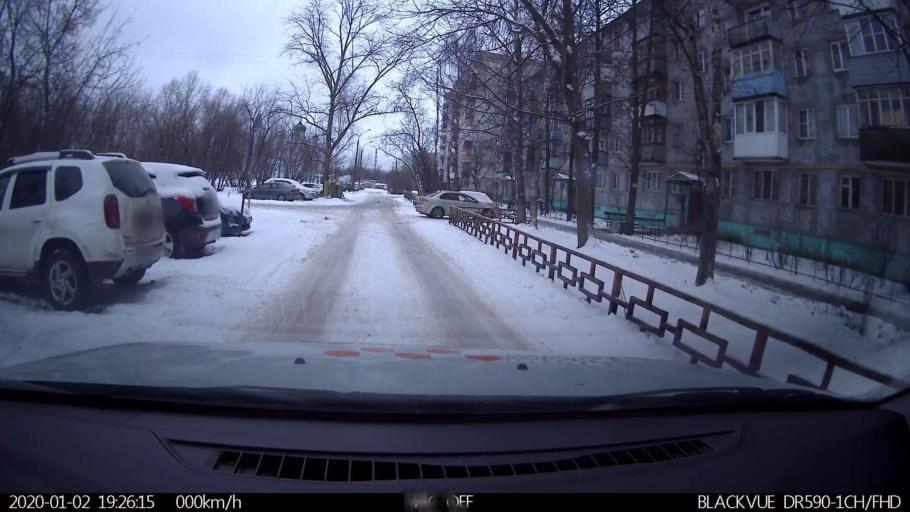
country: RU
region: Nizjnij Novgorod
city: Nizhniy Novgorod
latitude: 56.3187
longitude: 43.8751
